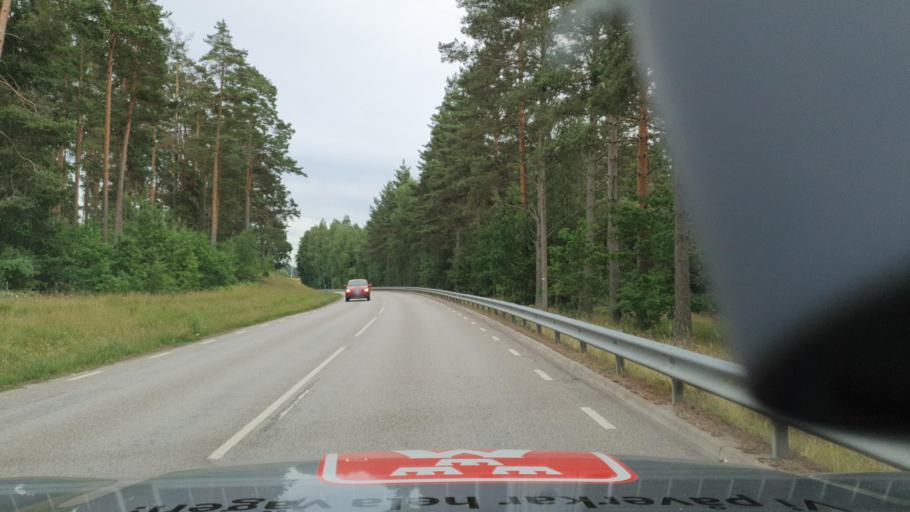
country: SE
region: Kalmar
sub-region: Nybro Kommun
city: Nybro
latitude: 56.7068
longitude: 15.9714
